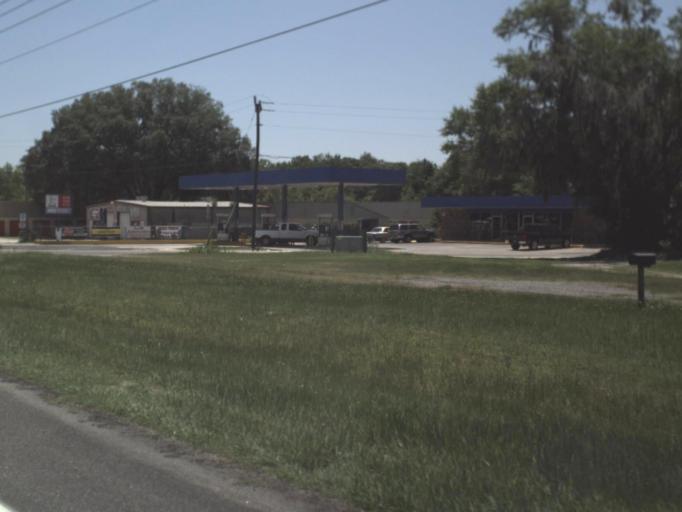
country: US
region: Florida
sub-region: Suwannee County
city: Live Oak
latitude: 30.3136
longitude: -83.0242
